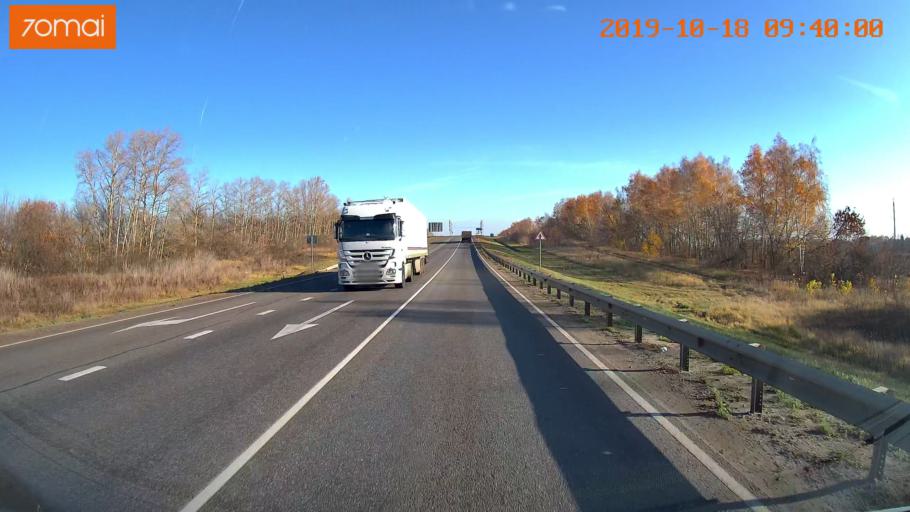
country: RU
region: Tula
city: Yefremov
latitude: 53.2593
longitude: 38.1423
